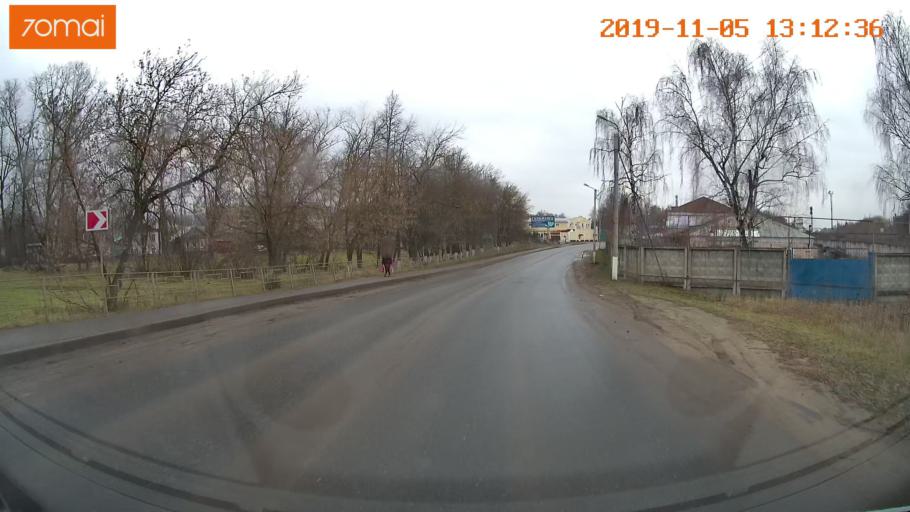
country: RU
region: Ivanovo
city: Shuya
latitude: 56.8566
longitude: 41.3525
